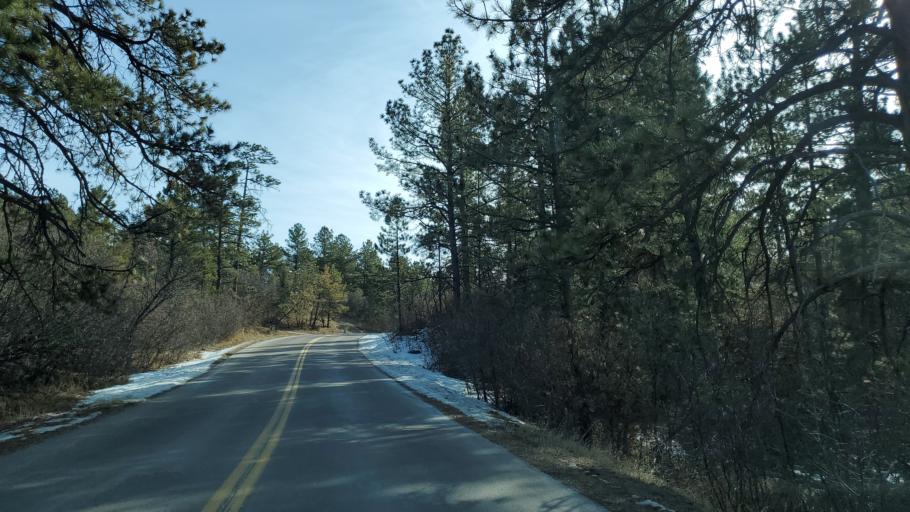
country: US
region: Colorado
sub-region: Douglas County
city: Castle Pines
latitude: 39.4350
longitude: -104.8752
